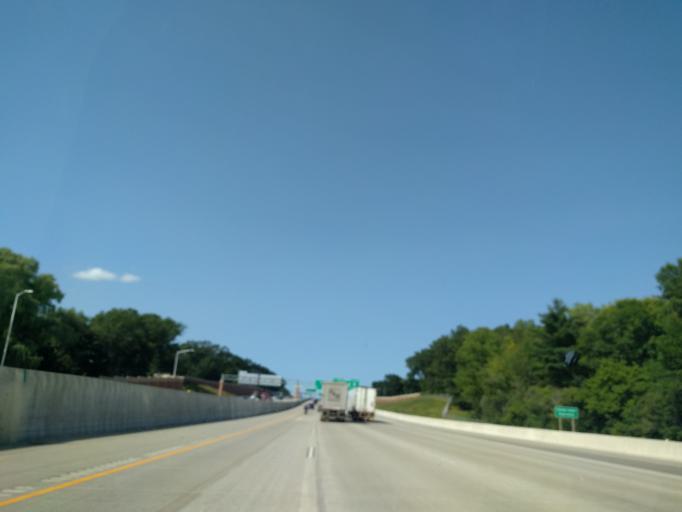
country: US
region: Wisconsin
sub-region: Brown County
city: Howard
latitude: 44.5131
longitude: -88.0825
